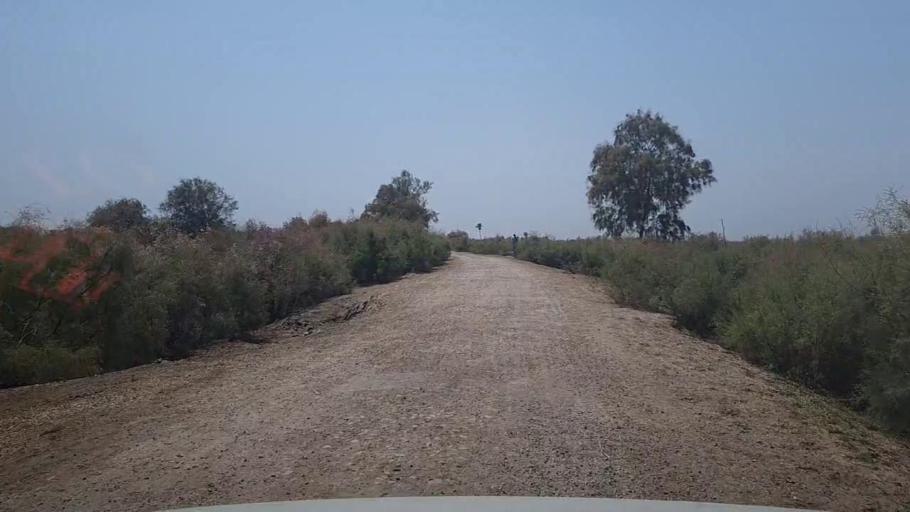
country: PK
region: Sindh
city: Kandhkot
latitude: 28.3084
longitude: 69.3572
